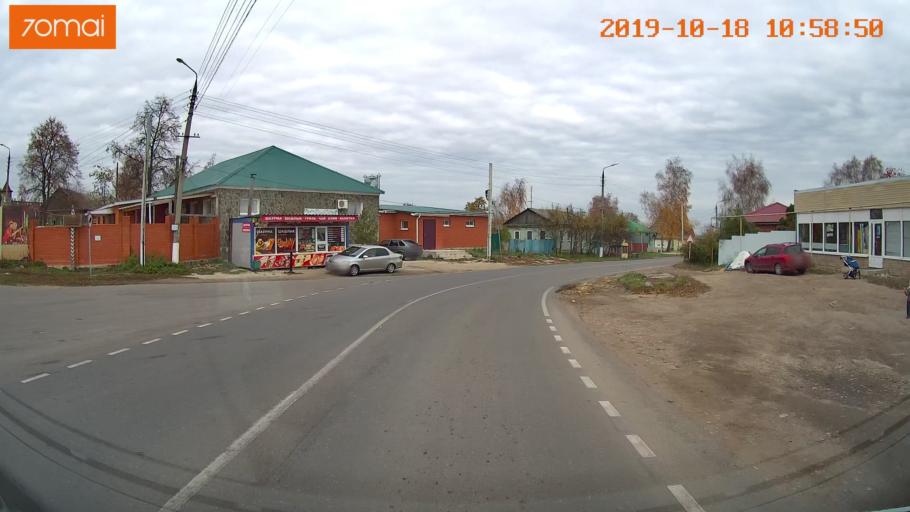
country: RU
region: Tula
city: Yepifan'
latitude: 53.8263
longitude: 38.5538
